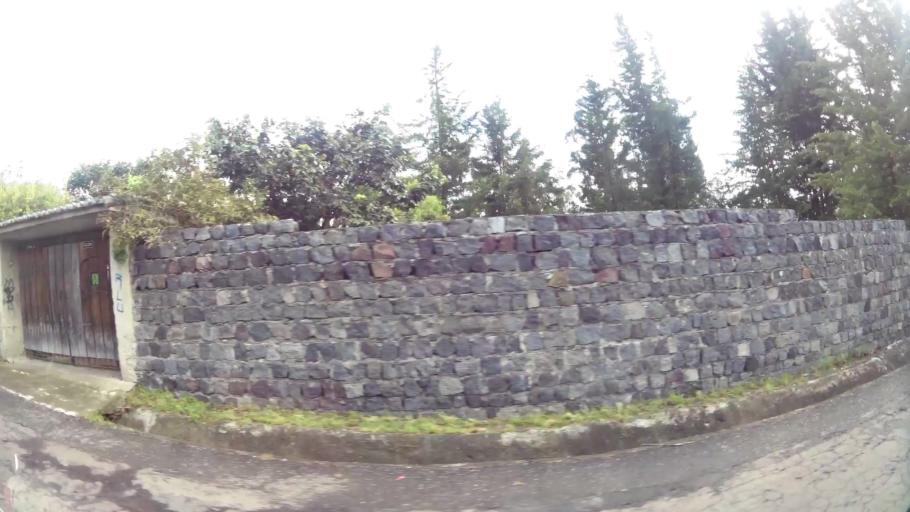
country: EC
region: Pichincha
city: Sangolqui
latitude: -0.3143
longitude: -78.4069
